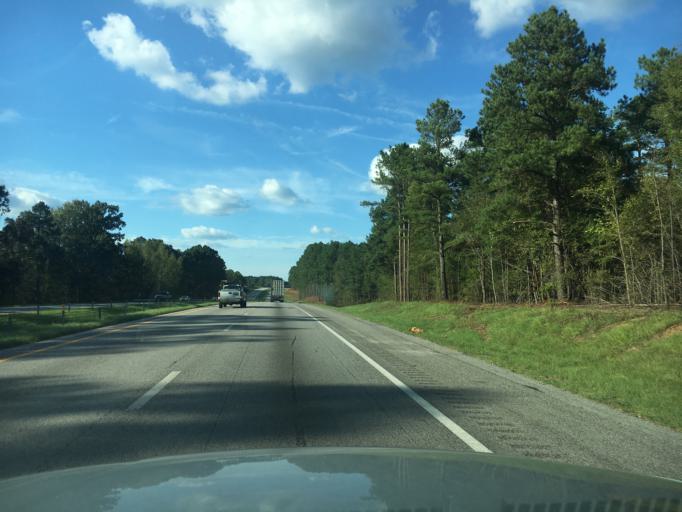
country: US
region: South Carolina
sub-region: Laurens County
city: Clinton
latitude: 34.5528
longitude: -81.8886
